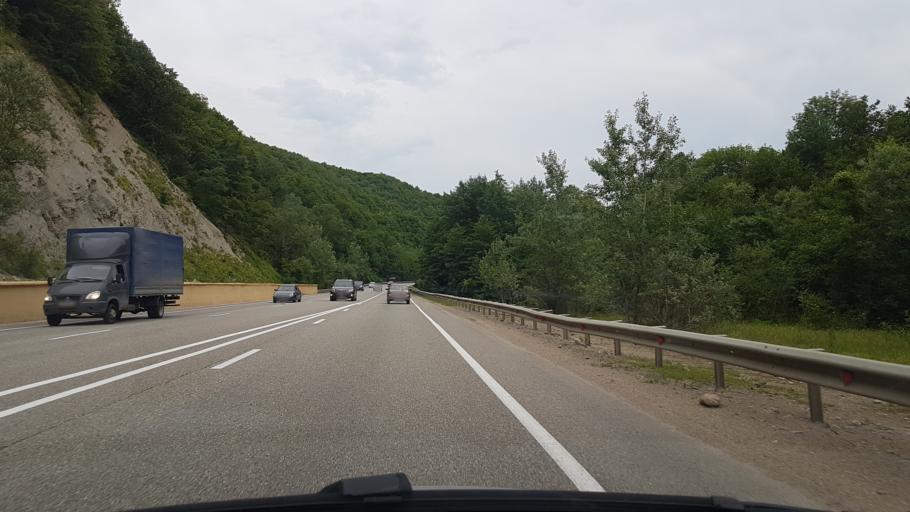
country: RU
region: Krasnodarskiy
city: Goryachiy Klyuch
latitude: 44.5706
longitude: 39.0020
